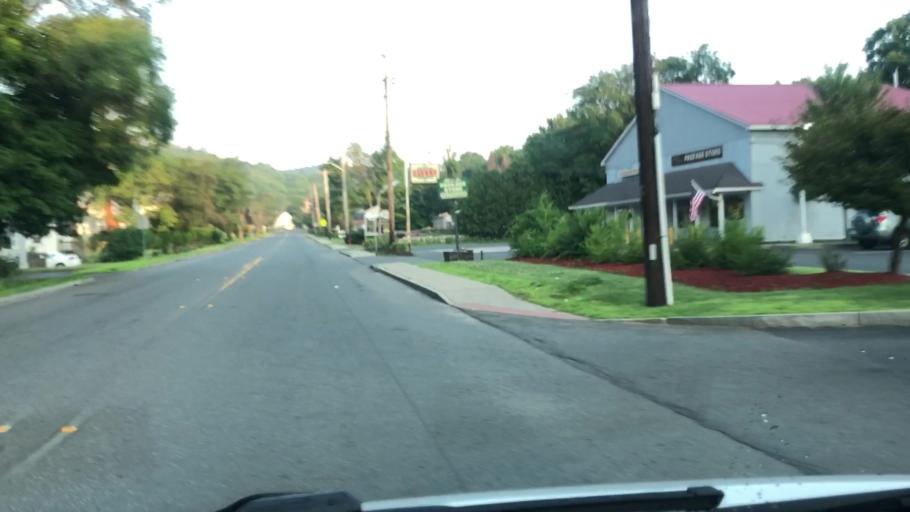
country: US
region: Massachusetts
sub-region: Hampshire County
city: Williamsburg
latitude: 42.3909
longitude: -72.7239
